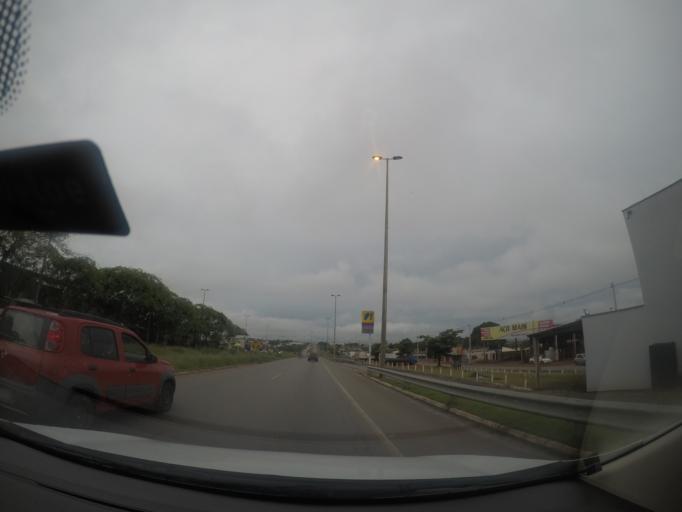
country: BR
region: Goias
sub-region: Aparecida De Goiania
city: Aparecida de Goiania
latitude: -16.7617
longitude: -49.3458
